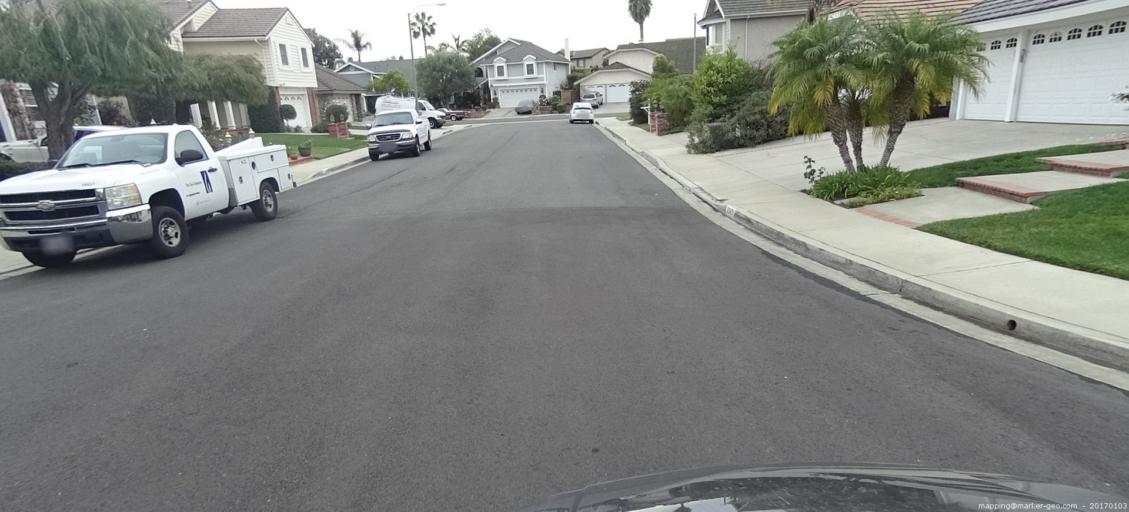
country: US
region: California
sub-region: Orange County
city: Dana Point
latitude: 33.4776
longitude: -117.6821
